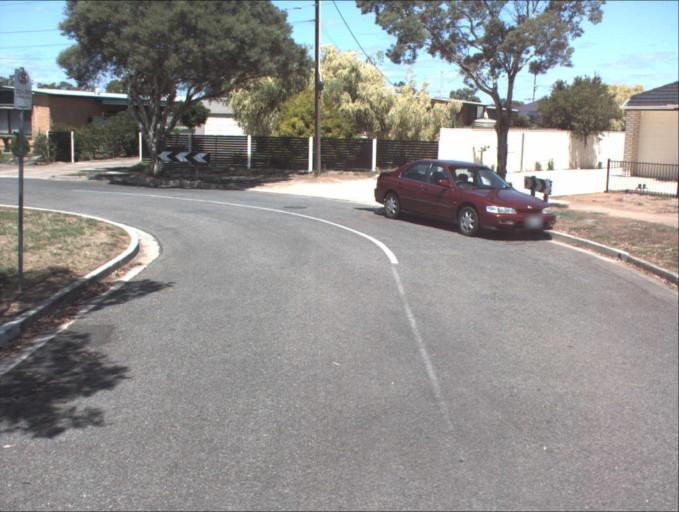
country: AU
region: South Australia
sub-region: Charles Sturt
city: Woodville North
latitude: -34.8542
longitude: 138.5530
